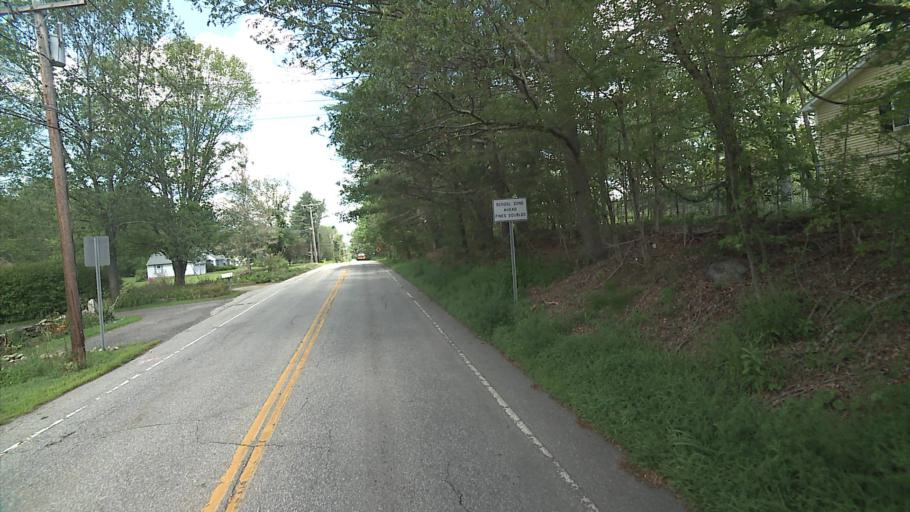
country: US
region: Connecticut
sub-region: Windham County
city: Windham
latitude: 41.7399
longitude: -72.1584
